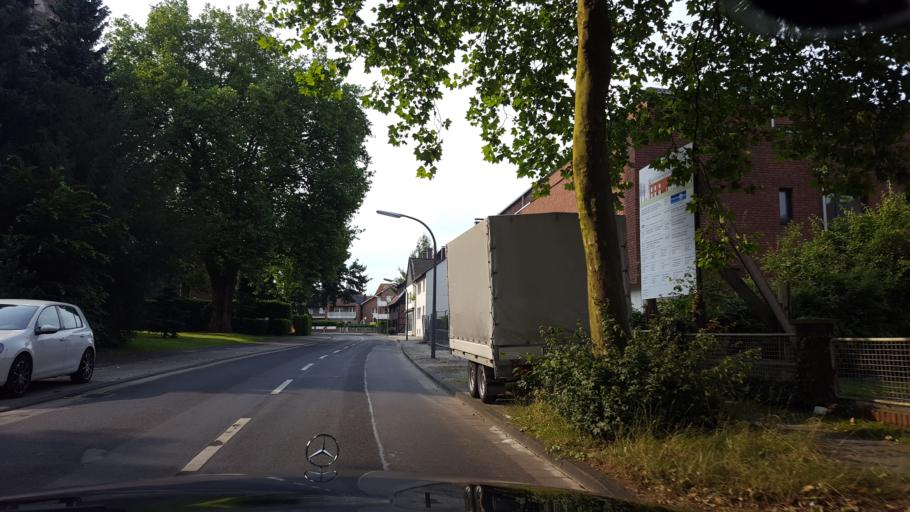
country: DE
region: North Rhine-Westphalia
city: Oer-Erkenschwick
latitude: 51.6110
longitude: 7.2634
